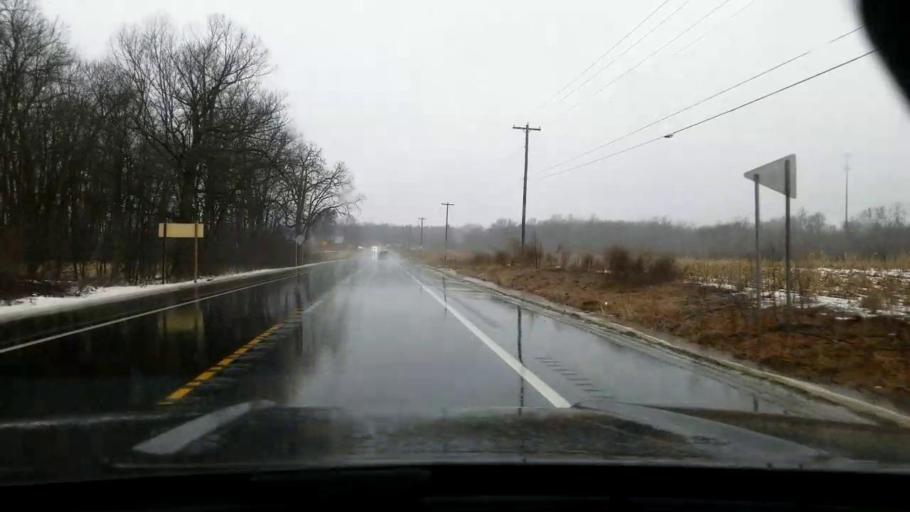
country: US
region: Michigan
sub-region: Jackson County
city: Napoleon
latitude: 42.1791
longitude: -84.2881
